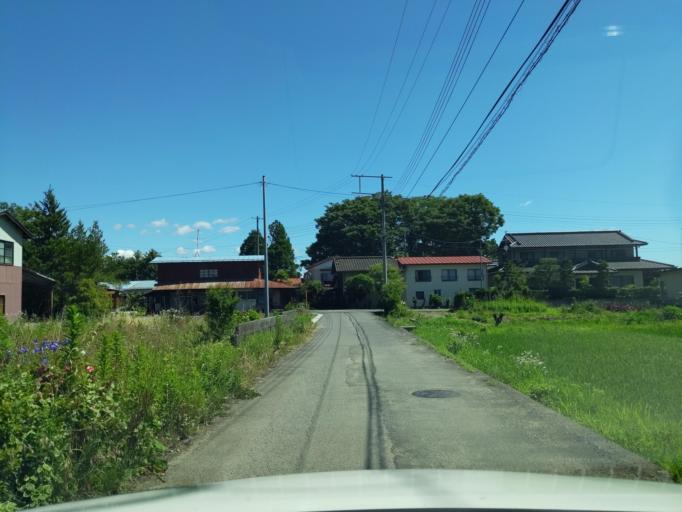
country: JP
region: Fukushima
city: Koriyama
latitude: 37.3885
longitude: 140.2839
